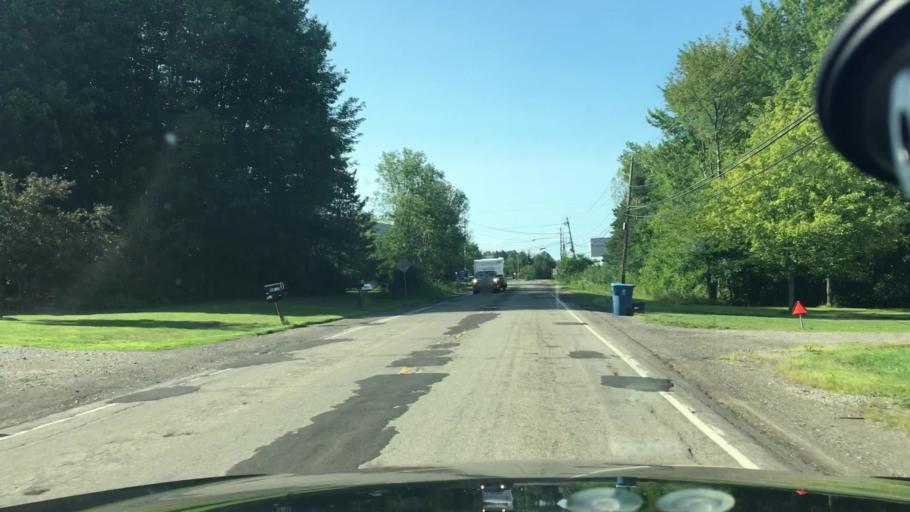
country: US
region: New York
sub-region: Erie County
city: Angola
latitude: 42.6269
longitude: -79.0267
